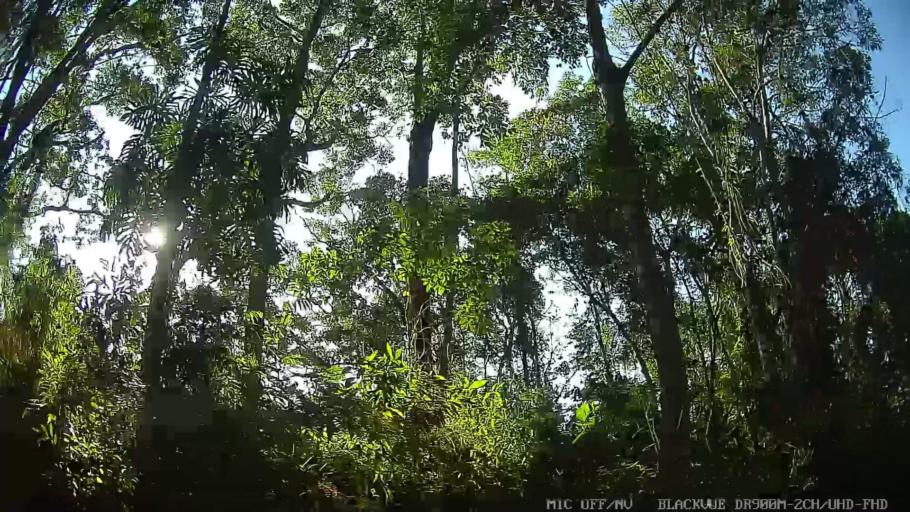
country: BR
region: Sao Paulo
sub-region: Guaruja
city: Guaruja
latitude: -23.9814
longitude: -46.2532
